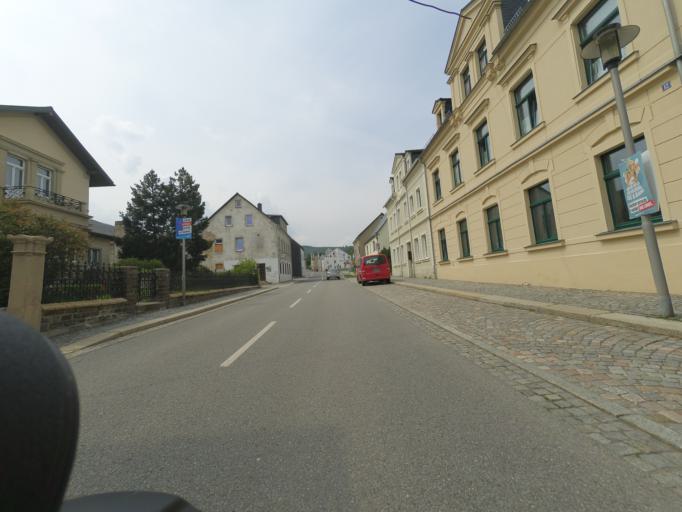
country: DE
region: Saxony
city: Olbernhau
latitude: 50.6608
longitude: 13.3320
